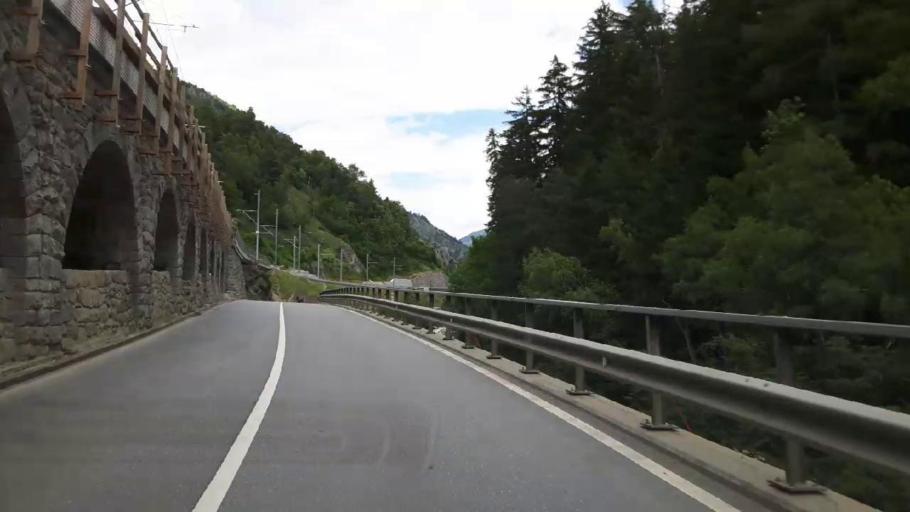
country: CH
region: Valais
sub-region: Goms District
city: Fiesch
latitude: 46.3662
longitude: 8.0640
